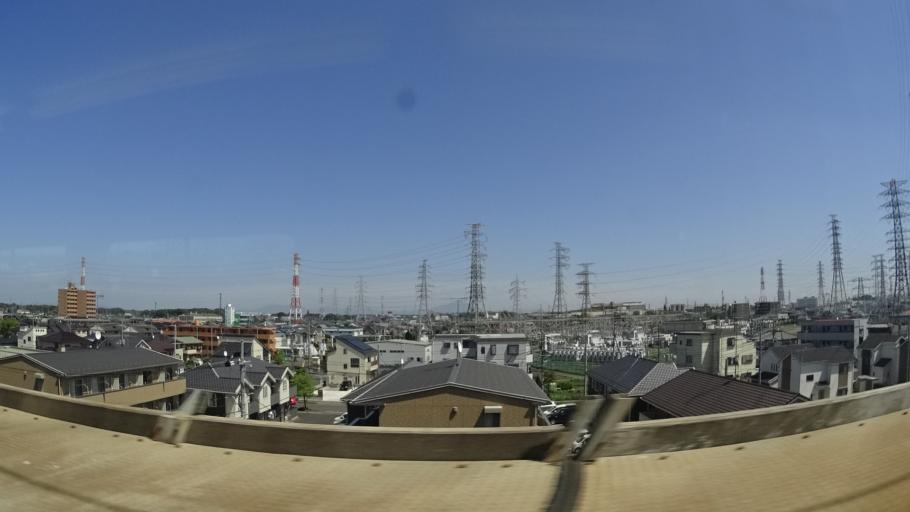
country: JP
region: Tochigi
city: Oyama
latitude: 36.3282
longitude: 139.8150
